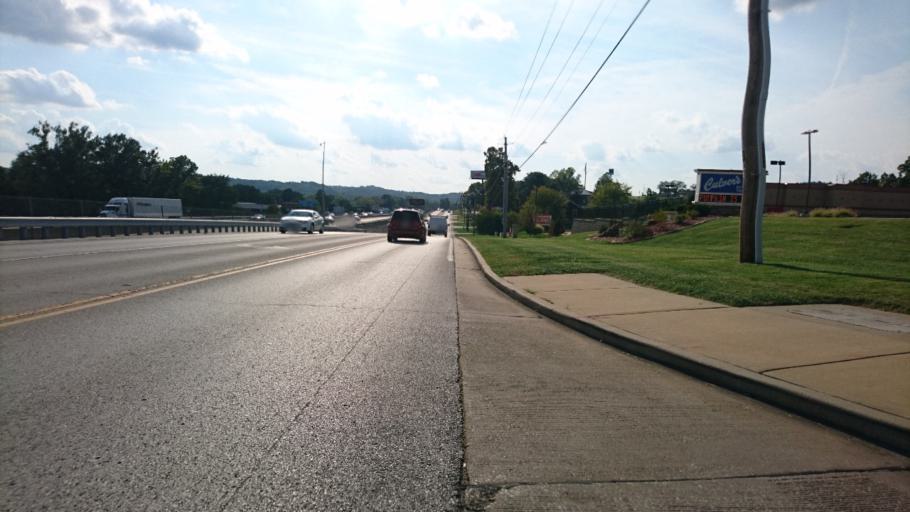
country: US
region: Missouri
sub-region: Saint Louis County
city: Eureka
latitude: 38.5064
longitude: -90.6335
